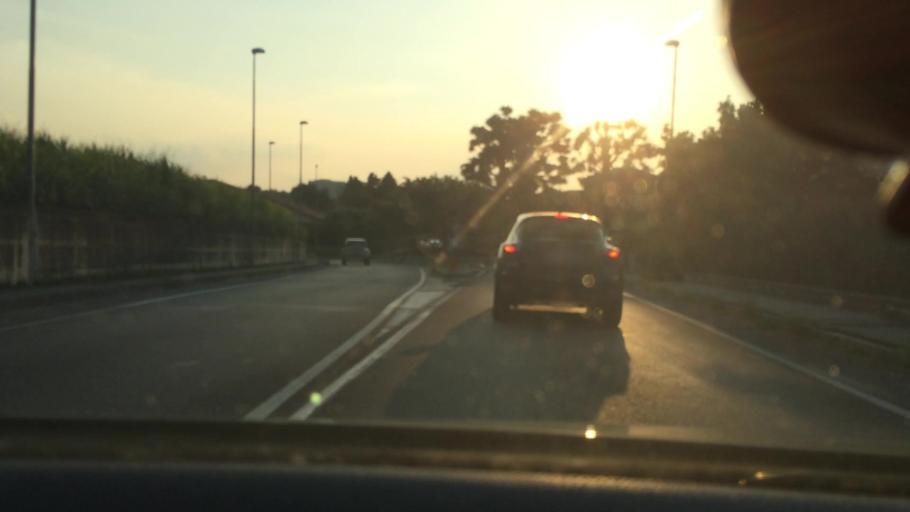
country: IT
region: Lombardy
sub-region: Provincia di Lecco
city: Brivio
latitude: 45.7344
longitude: 9.4280
